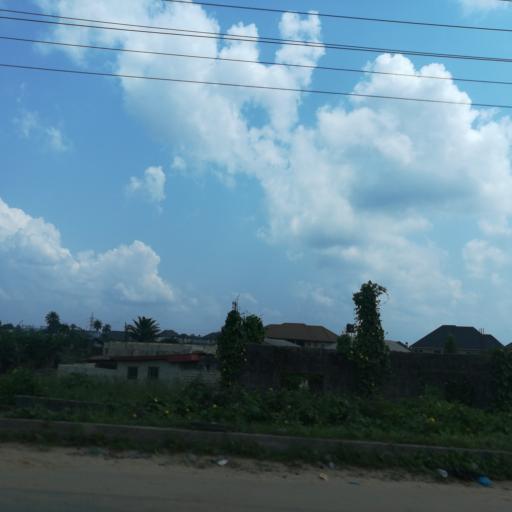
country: NG
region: Rivers
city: Port Harcourt
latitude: 4.8413
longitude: 7.0807
